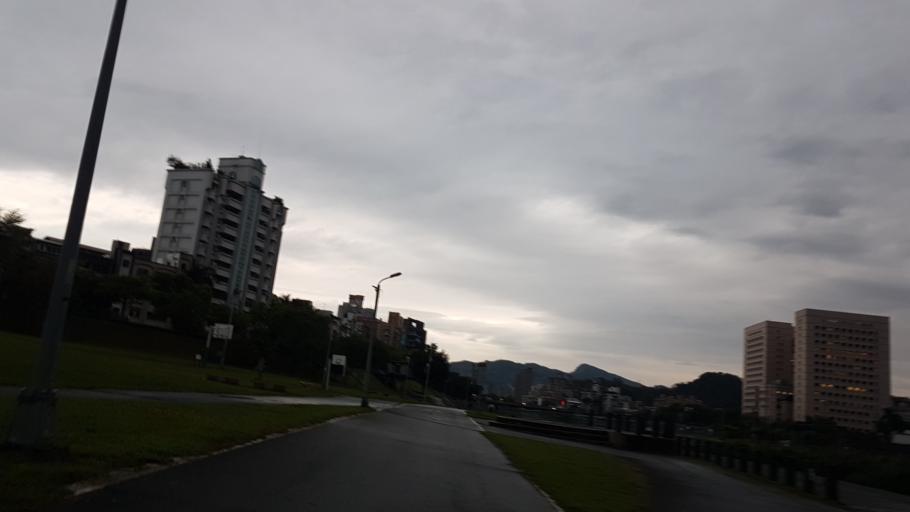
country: TW
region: Taipei
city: Taipei
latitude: 24.9827
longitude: 121.5712
